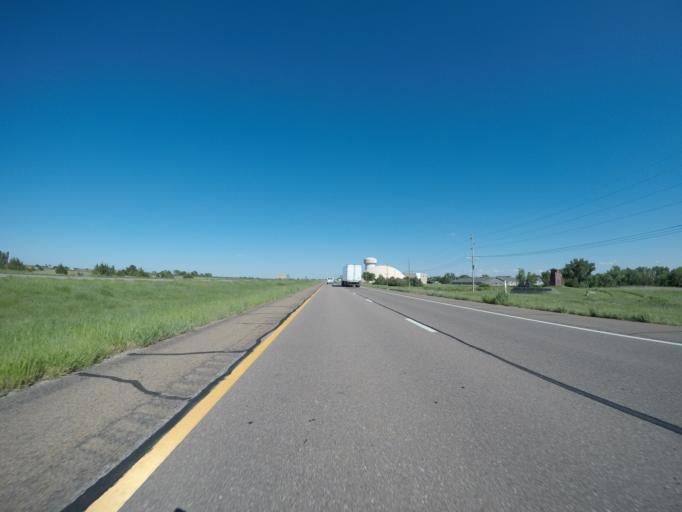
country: US
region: Kansas
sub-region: Ellis County
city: Hays
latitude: 38.8917
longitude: -99.3029
